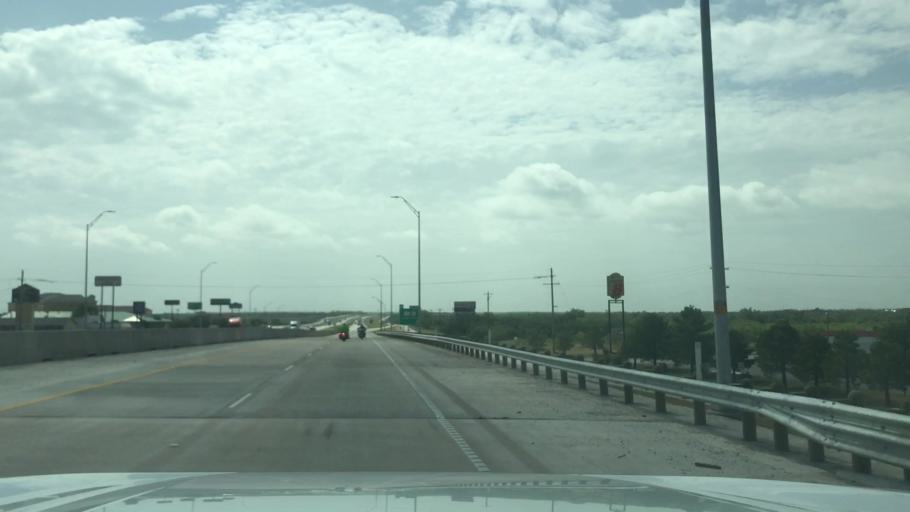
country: US
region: Texas
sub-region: Taylor County
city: Abilene
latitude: 32.4770
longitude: -99.6994
